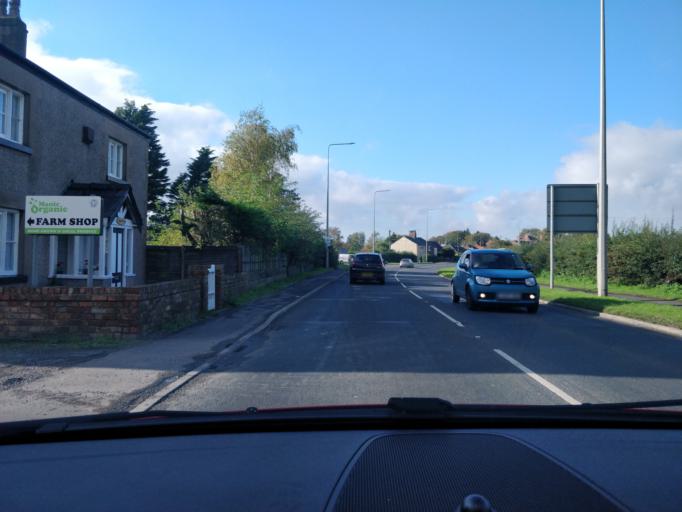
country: GB
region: England
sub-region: Lancashire
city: Ormskirk
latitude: 53.6111
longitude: -2.9366
